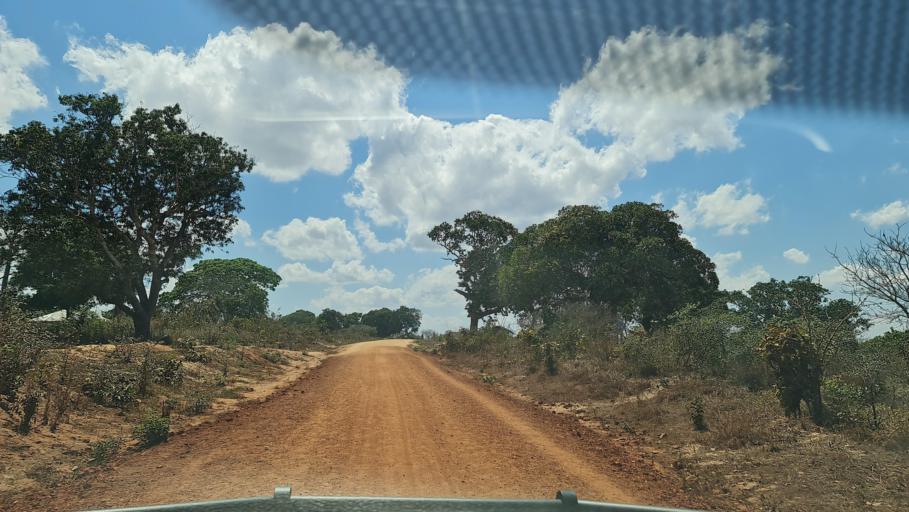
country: MZ
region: Nampula
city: Nacala
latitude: -14.1757
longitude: 40.2128
